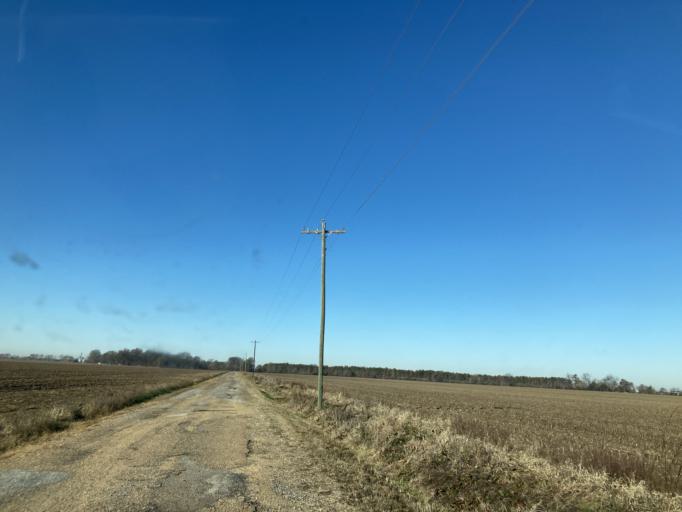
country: US
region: Mississippi
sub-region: Yazoo County
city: Yazoo City
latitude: 32.9226
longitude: -90.5944
